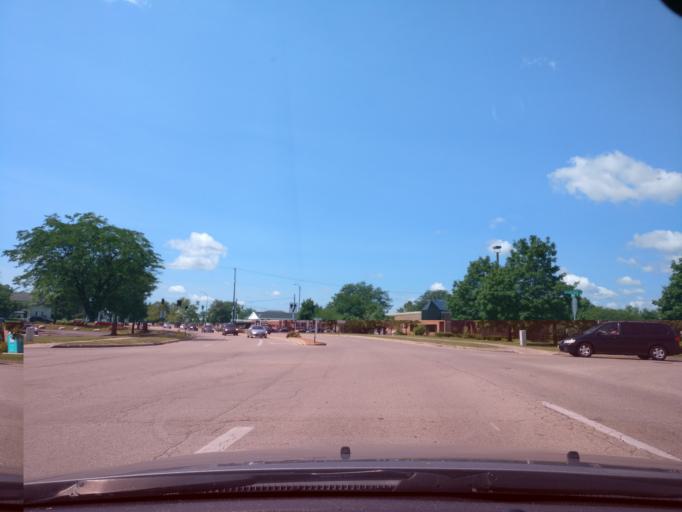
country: US
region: Ohio
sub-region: Montgomery County
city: Centerville
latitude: 39.6305
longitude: -84.1921
